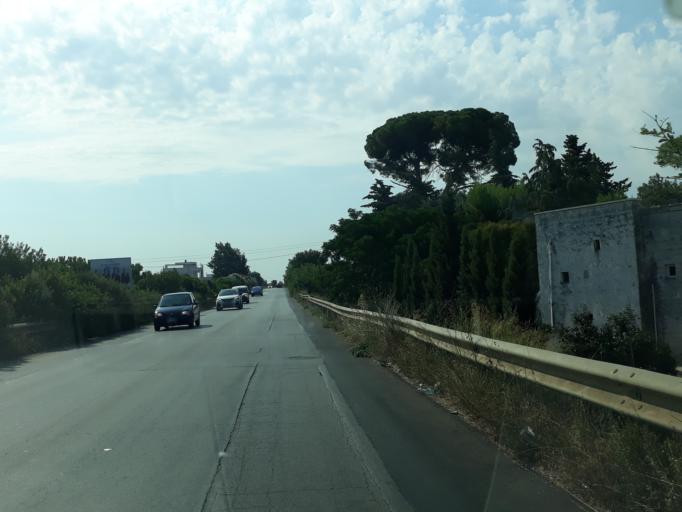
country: IT
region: Apulia
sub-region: Provincia di Brindisi
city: Carovigno
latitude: 40.6979
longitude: 17.6664
